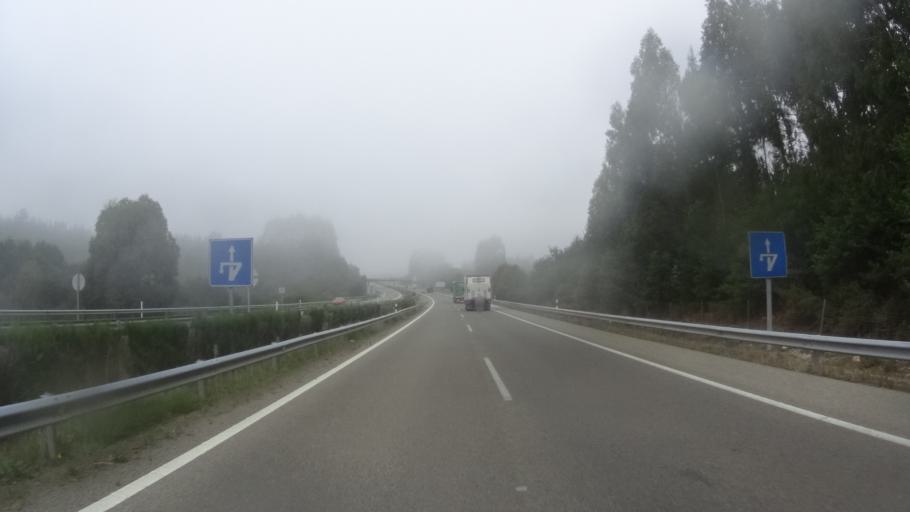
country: ES
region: Galicia
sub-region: Provincia de Lugo
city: Guitiriz
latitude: 43.1813
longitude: -7.8134
